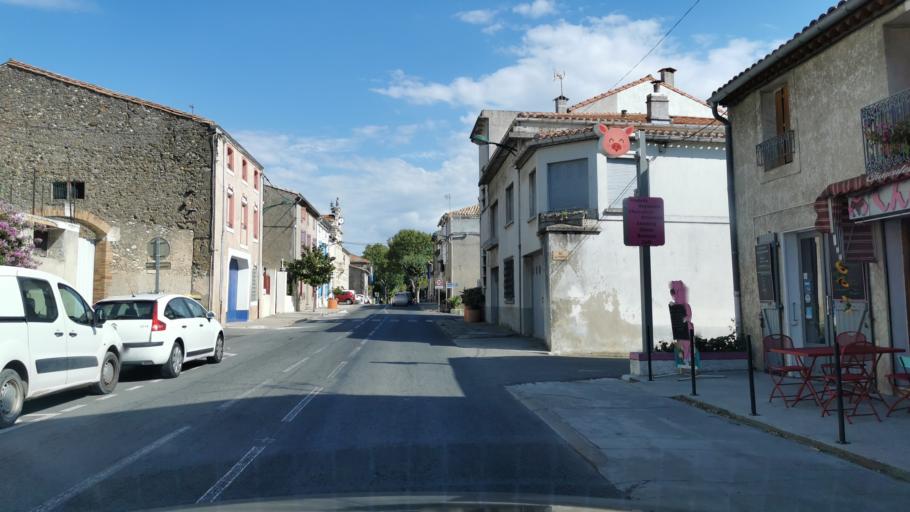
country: FR
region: Languedoc-Roussillon
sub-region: Departement de l'Aude
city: Azille
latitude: 43.2508
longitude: 2.6552
